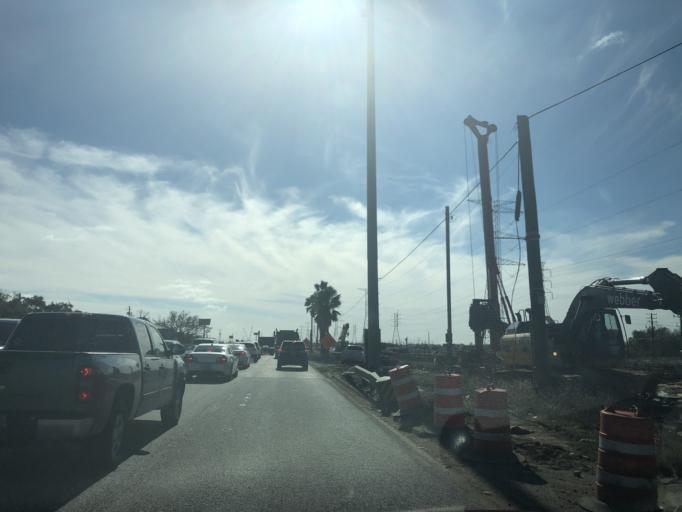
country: US
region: Texas
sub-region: Harris County
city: Seabrook
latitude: 29.5647
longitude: -95.0270
